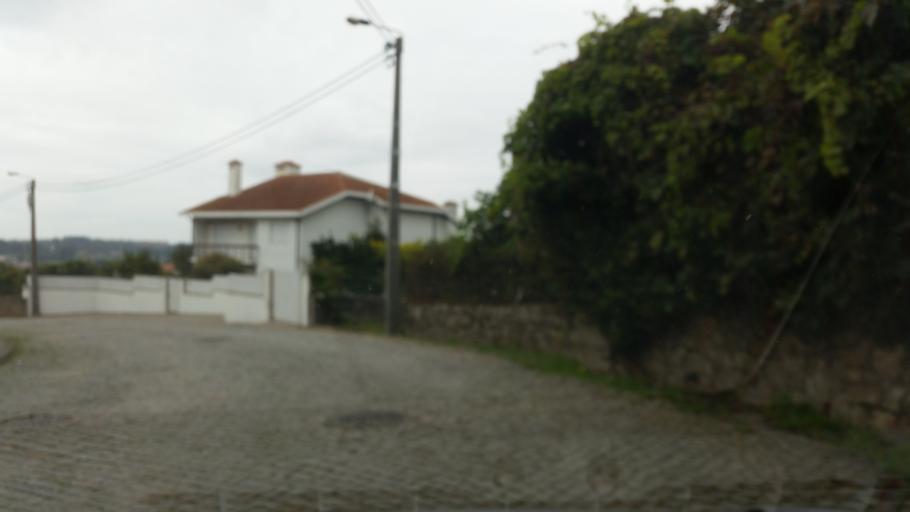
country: PT
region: Porto
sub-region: Valongo
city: Alfena
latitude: 41.2439
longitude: -8.5438
